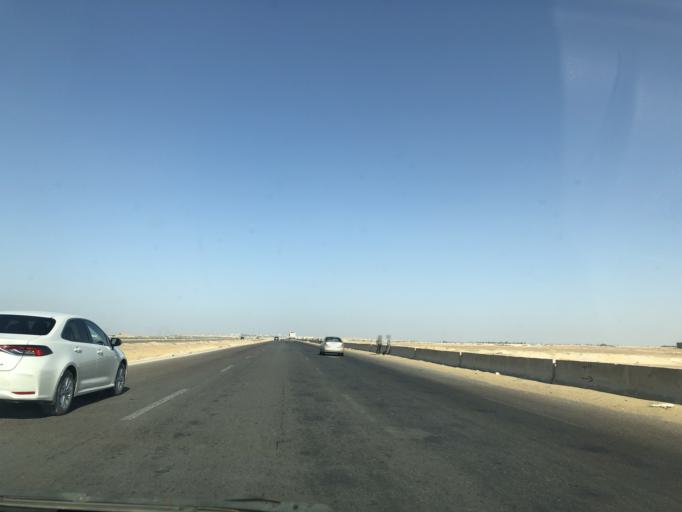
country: EG
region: Muhafazat al Minufiyah
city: Ashmun
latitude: 30.0677
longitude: 30.8848
